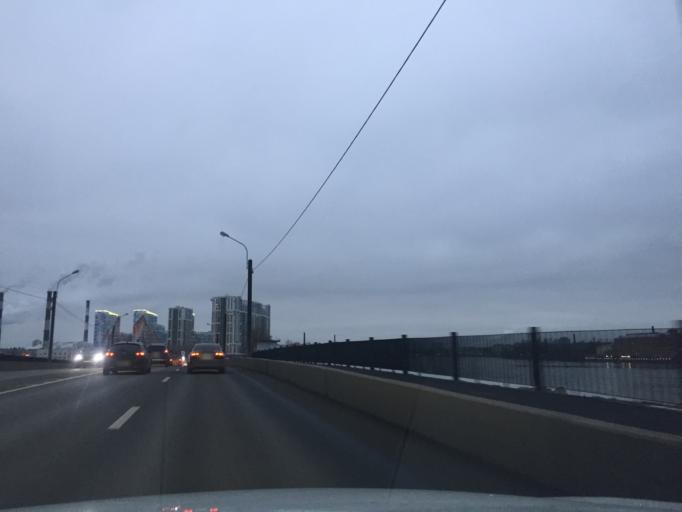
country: RU
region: St.-Petersburg
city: Obukhovo
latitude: 59.9004
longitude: 30.4417
